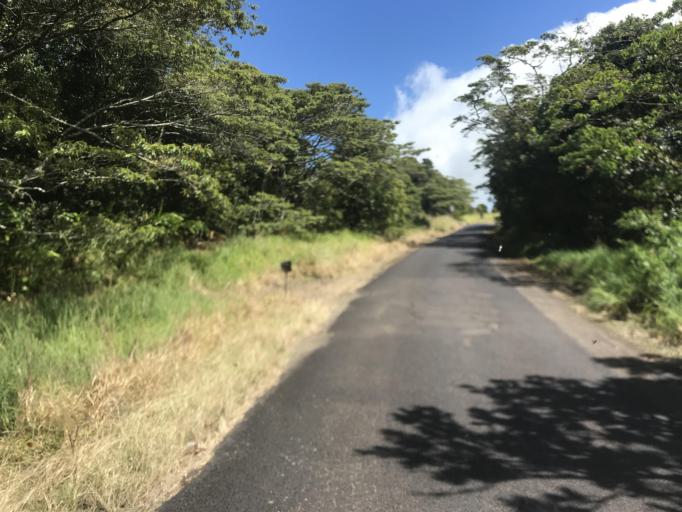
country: AU
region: Queensland
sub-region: Tablelands
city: Ravenshoe
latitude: -17.5198
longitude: 145.5635
